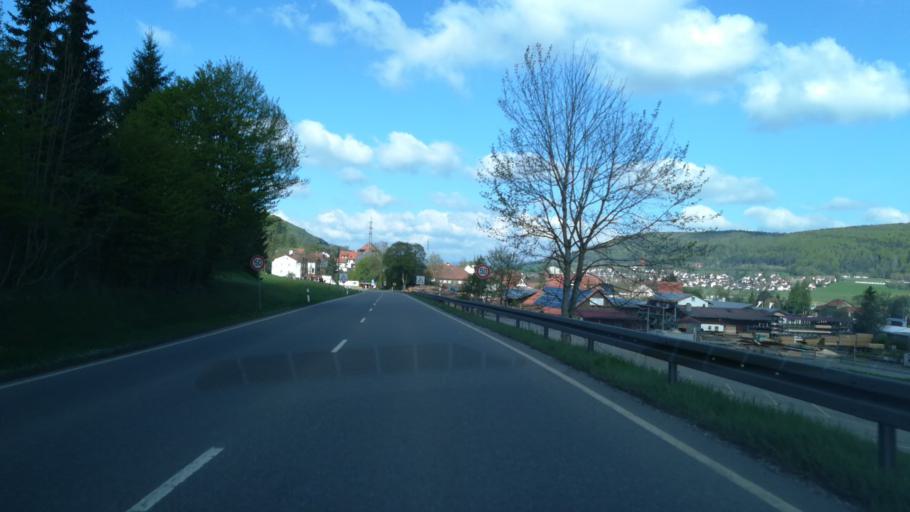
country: DE
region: Baden-Wuerttemberg
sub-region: Freiburg Region
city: Blumberg
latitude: 47.8355
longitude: 8.5610
